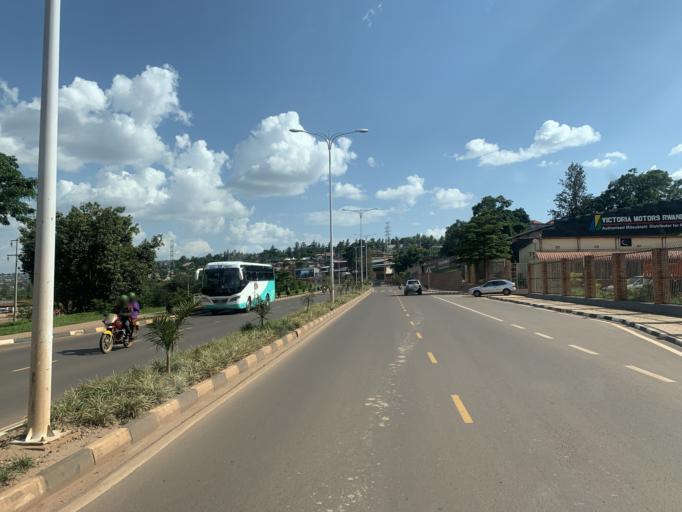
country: RW
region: Kigali
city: Kigali
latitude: -1.9608
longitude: 30.0771
